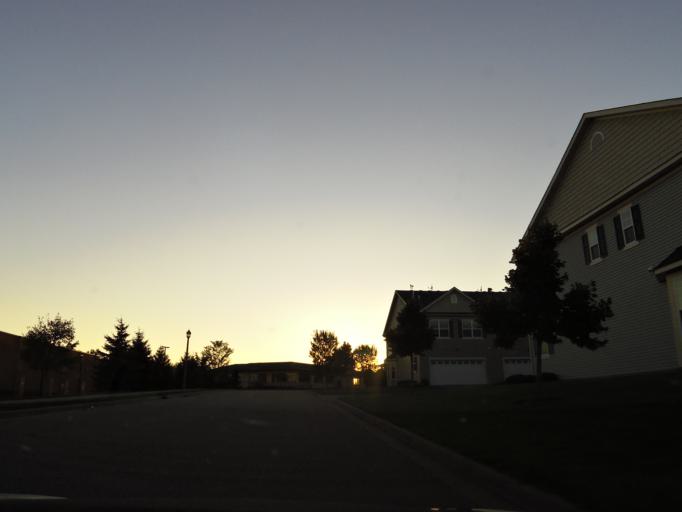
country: US
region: Minnesota
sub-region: Washington County
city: Oakdale
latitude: 44.9653
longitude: -92.9507
